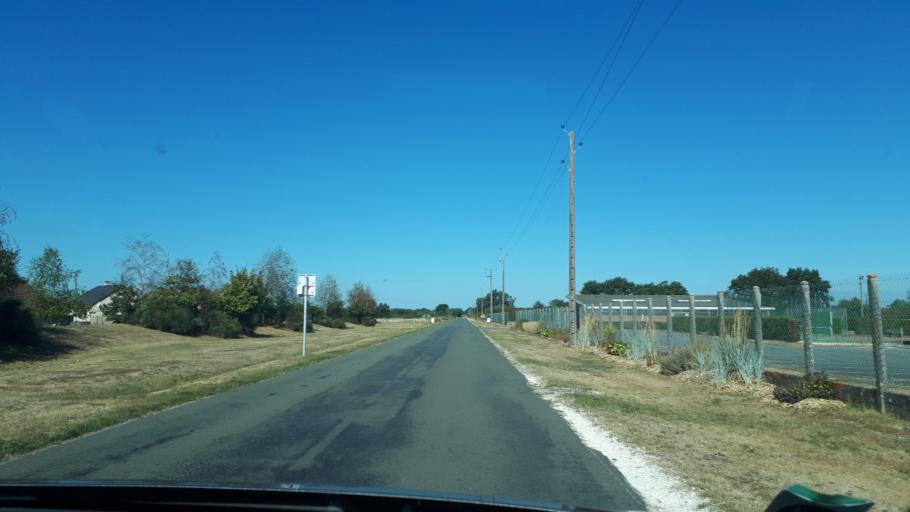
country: FR
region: Centre
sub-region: Departement du Loiret
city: Coullons
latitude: 47.6263
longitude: 2.4863
